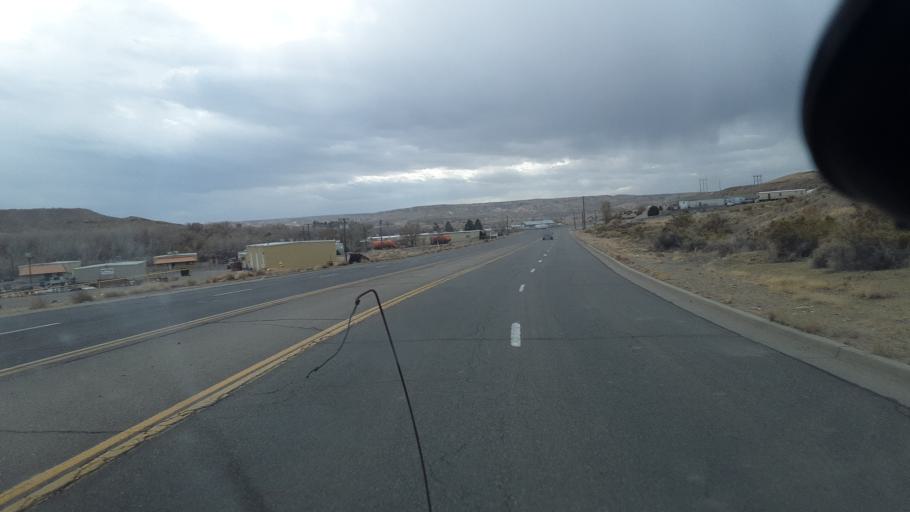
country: US
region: New Mexico
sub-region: San Juan County
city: Farmington
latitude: 36.7464
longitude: -108.2455
